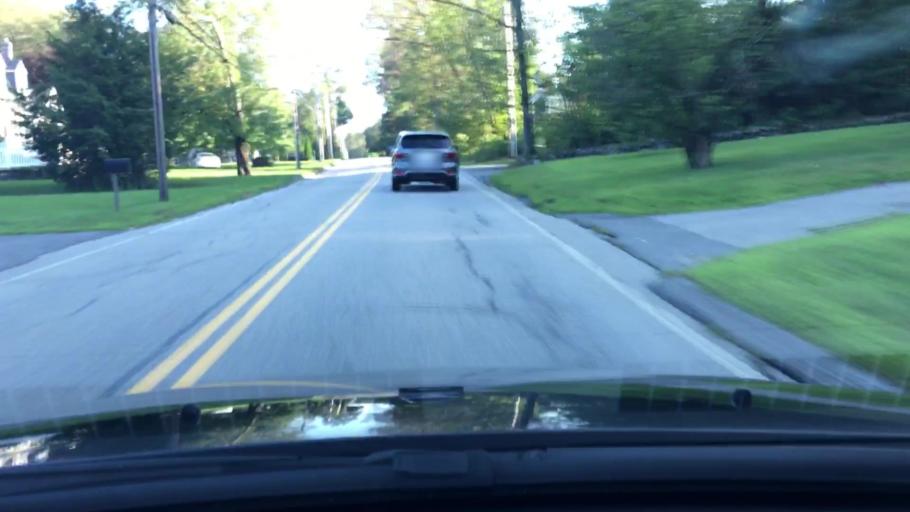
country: US
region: Massachusetts
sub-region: Worcester County
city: West Boylston
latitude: 42.3550
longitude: -71.7786
